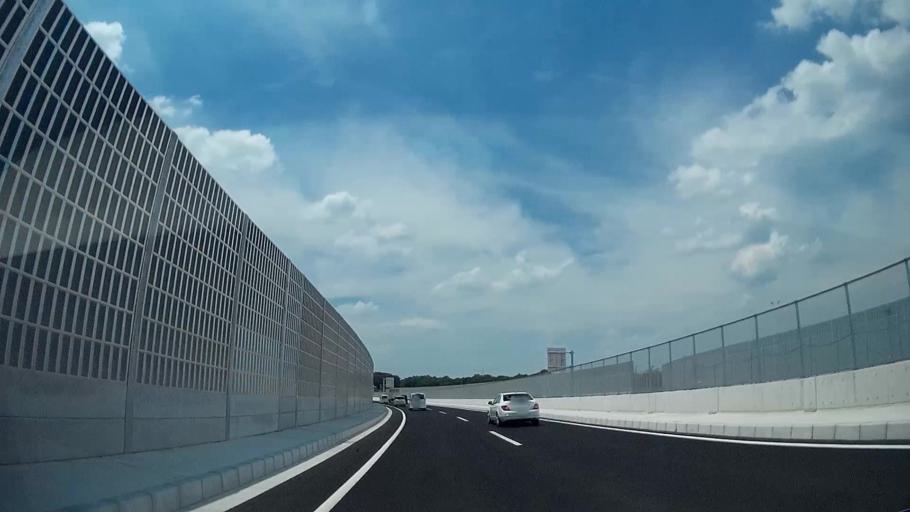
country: JP
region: Chiba
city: Matsudo
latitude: 35.7552
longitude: 139.9171
